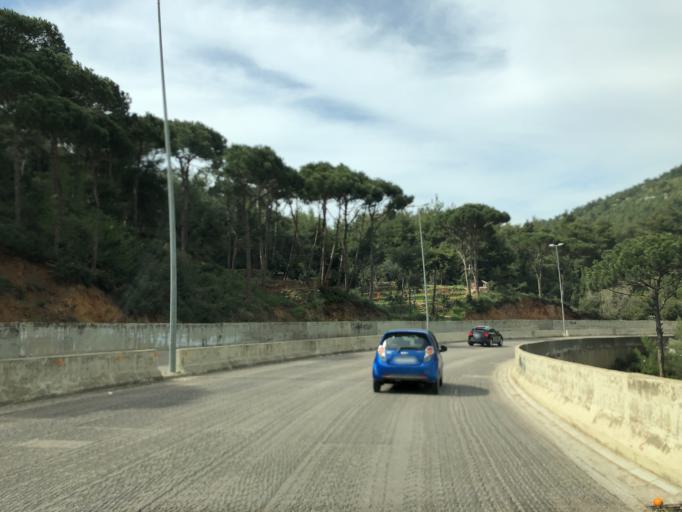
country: LB
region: Mont-Liban
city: Bhamdoun el Mhatta
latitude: 33.8923
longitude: 35.6577
